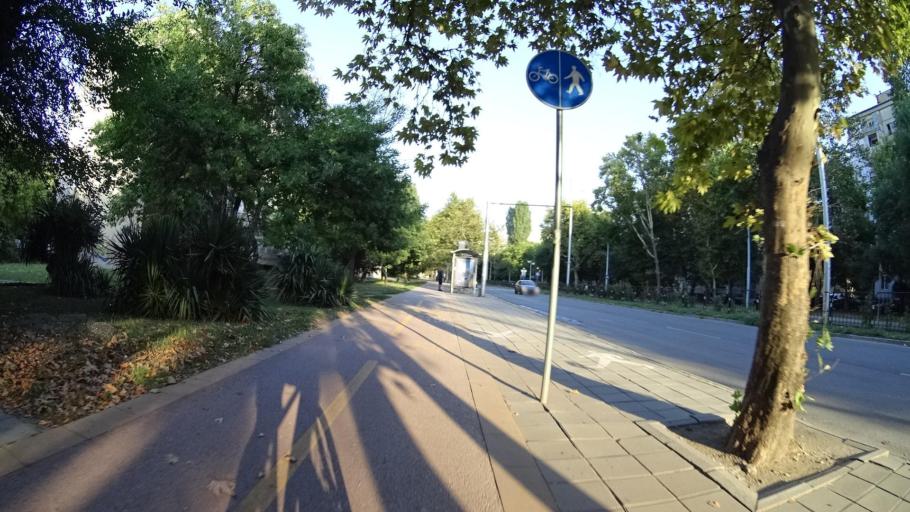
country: BG
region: Plovdiv
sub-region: Obshtina Plovdiv
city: Plovdiv
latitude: 42.1282
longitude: 24.7269
